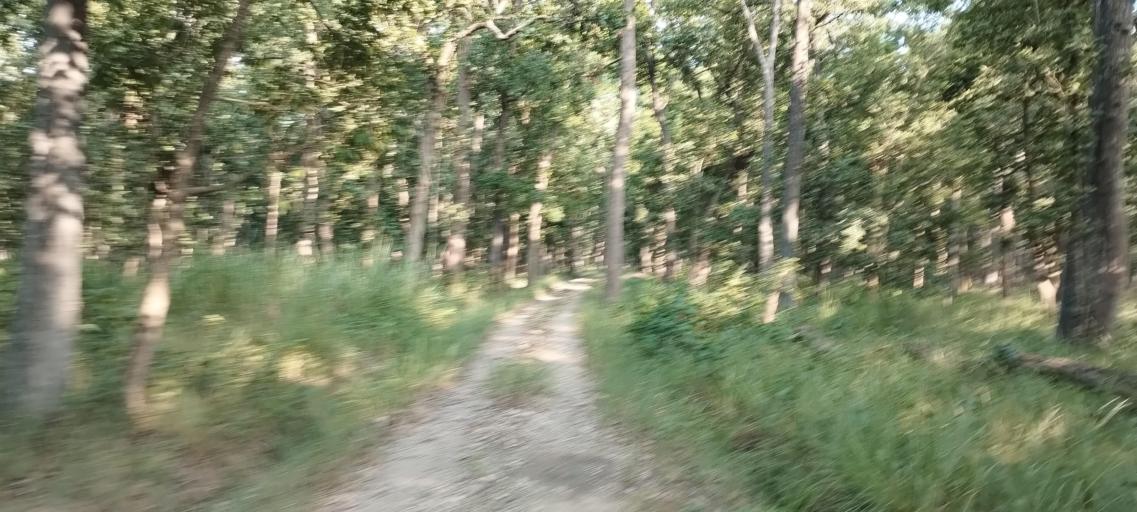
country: NP
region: Far Western
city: Tikapur
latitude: 28.5193
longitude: 81.2786
